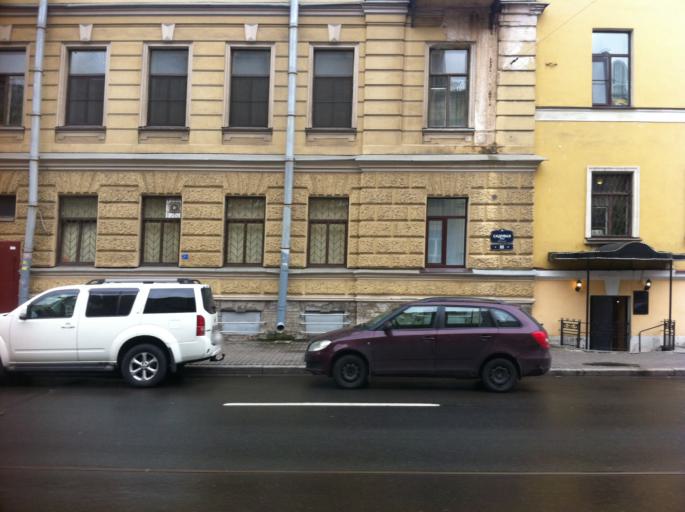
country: RU
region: St.-Petersburg
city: Admiralteisky
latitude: 59.9192
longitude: 30.2930
